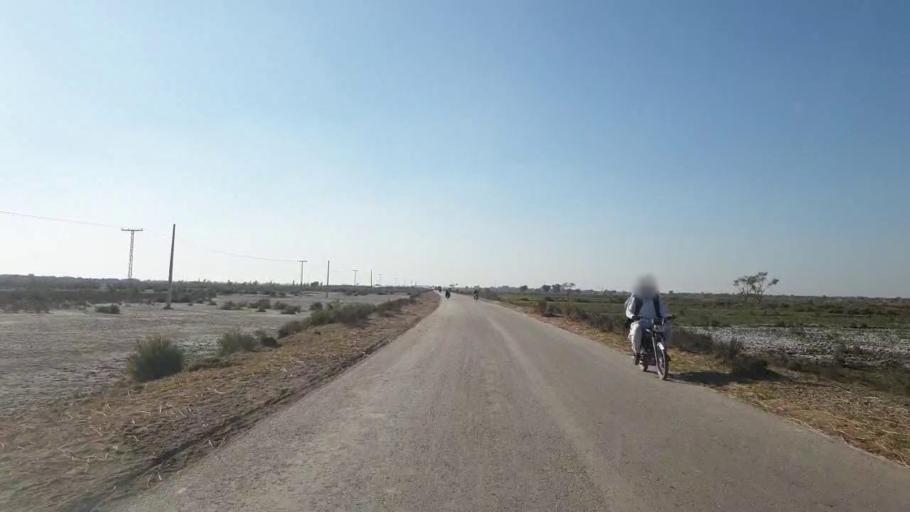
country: PK
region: Sindh
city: New Badah
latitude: 27.3249
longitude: 68.0615
